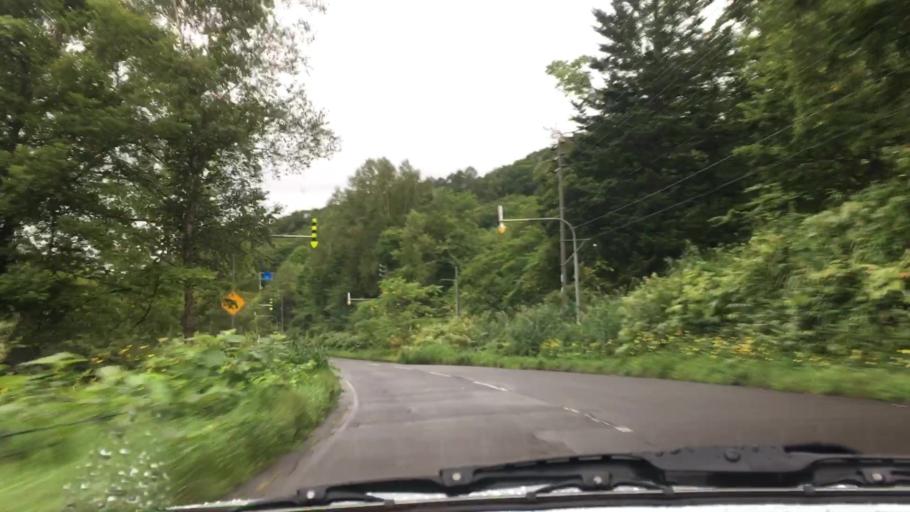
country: JP
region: Hokkaido
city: Niseko Town
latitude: 42.6620
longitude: 140.7661
